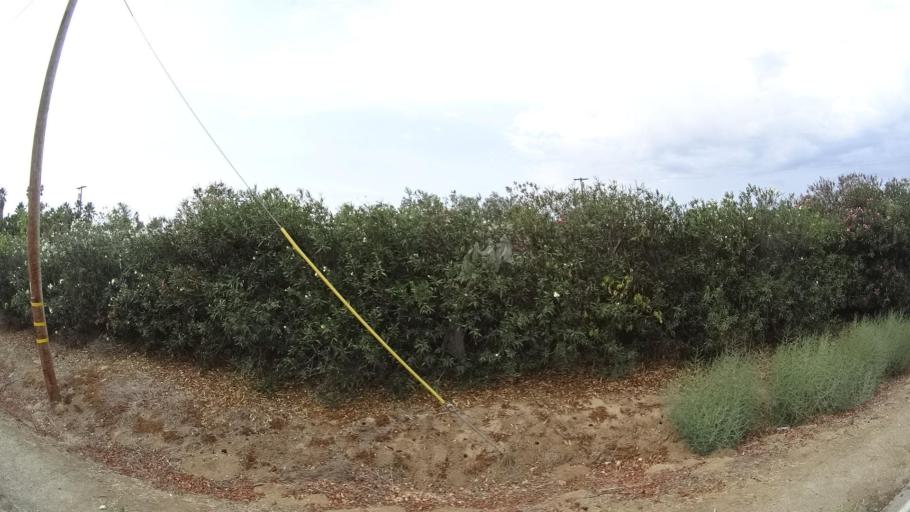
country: US
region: California
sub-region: San Diego County
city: Ramona
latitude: 33.0630
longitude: -116.8609
